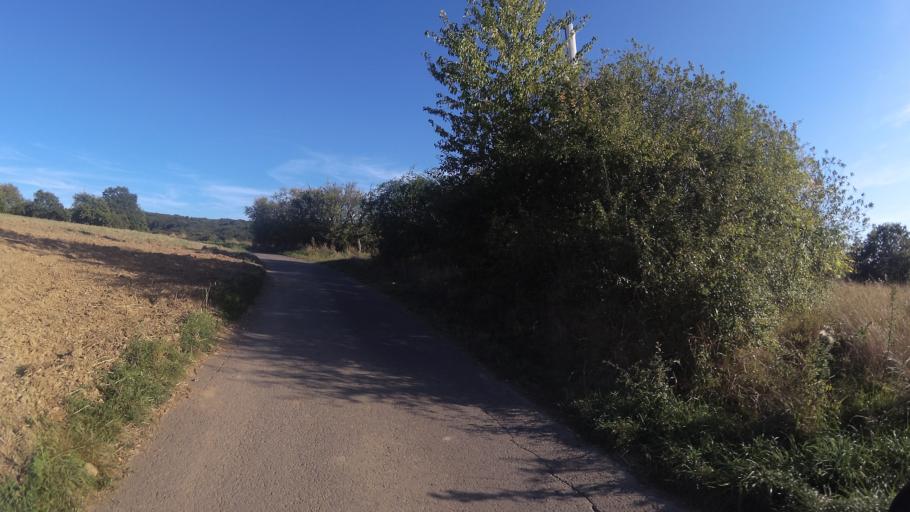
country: DE
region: Saarland
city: Marpingen
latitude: 49.4671
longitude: 7.0733
